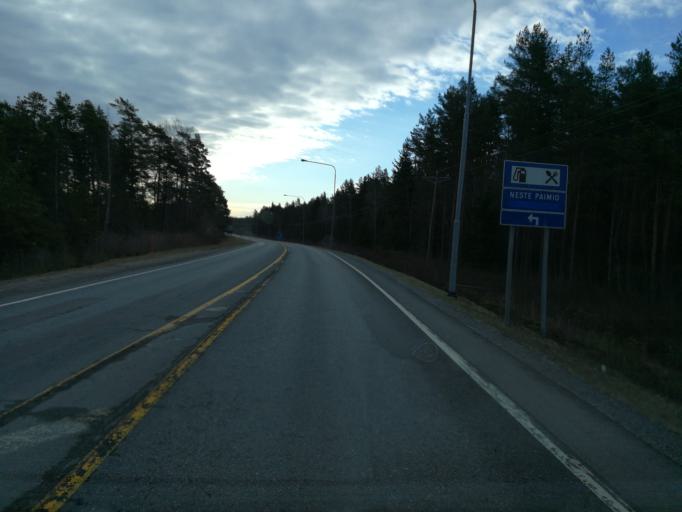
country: FI
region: Varsinais-Suomi
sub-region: Turku
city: Paimio
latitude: 60.4216
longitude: 22.7188
